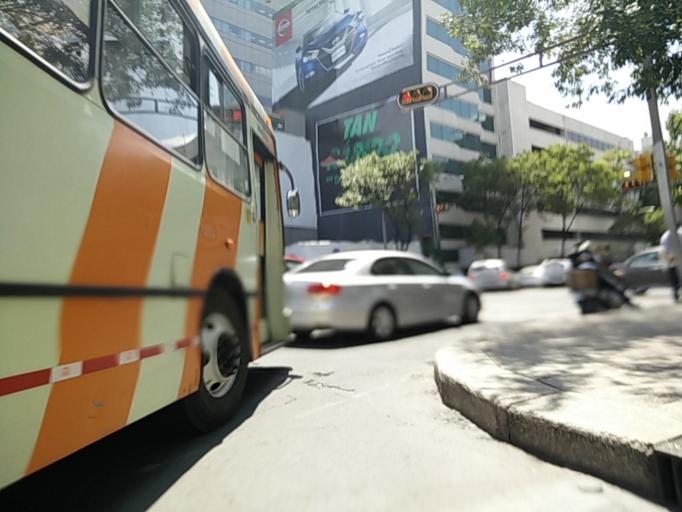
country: MX
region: Mexico City
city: Polanco
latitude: 19.4248
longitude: -99.1716
